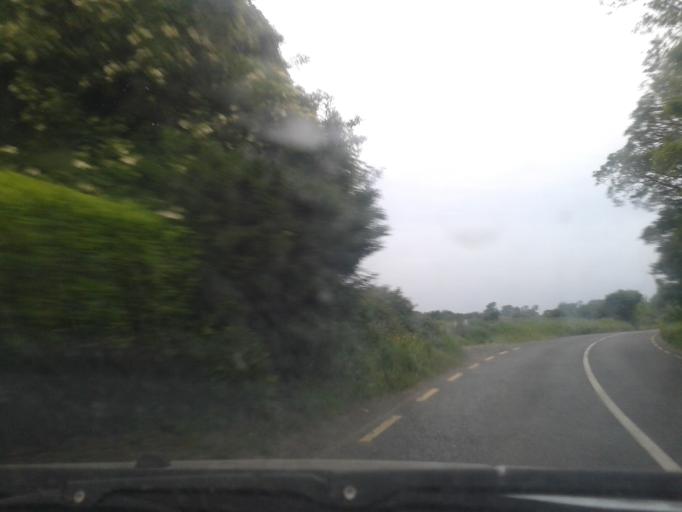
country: IE
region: Leinster
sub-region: Dublin City
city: Finglas
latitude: 53.4110
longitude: -6.3069
